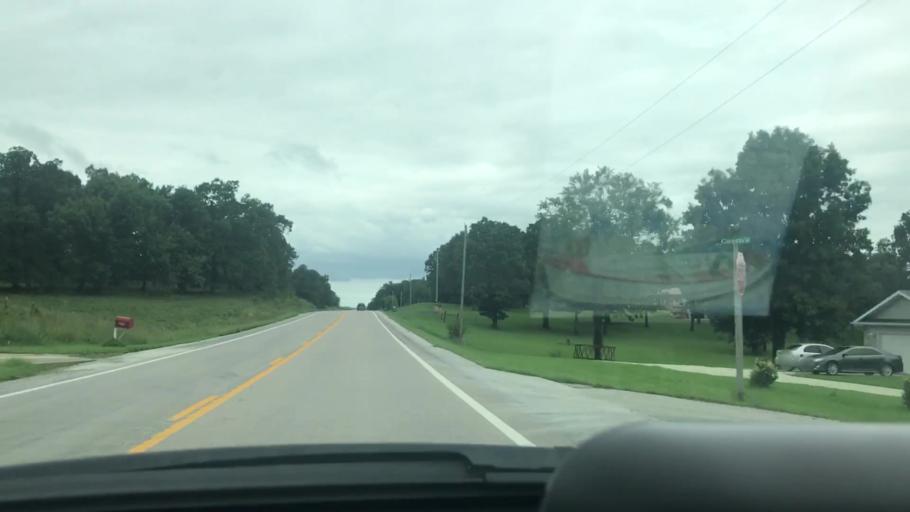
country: US
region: Missouri
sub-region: Dallas County
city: Buffalo
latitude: 37.7095
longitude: -93.1138
